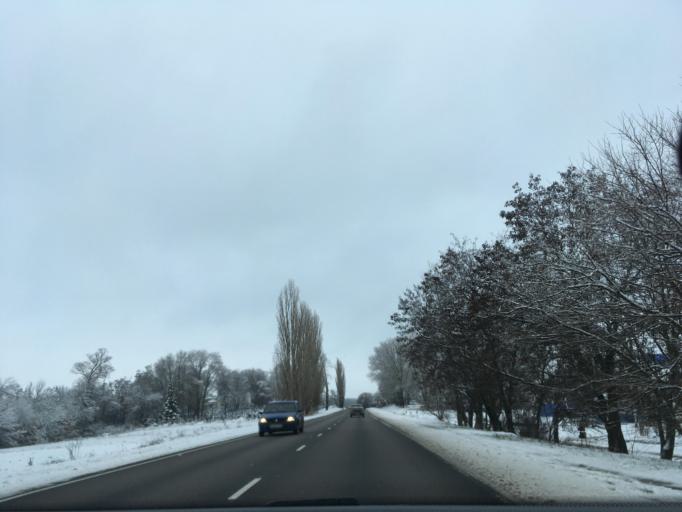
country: RU
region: Voronezj
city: Zabolotovka
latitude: 50.2468
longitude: 39.3654
